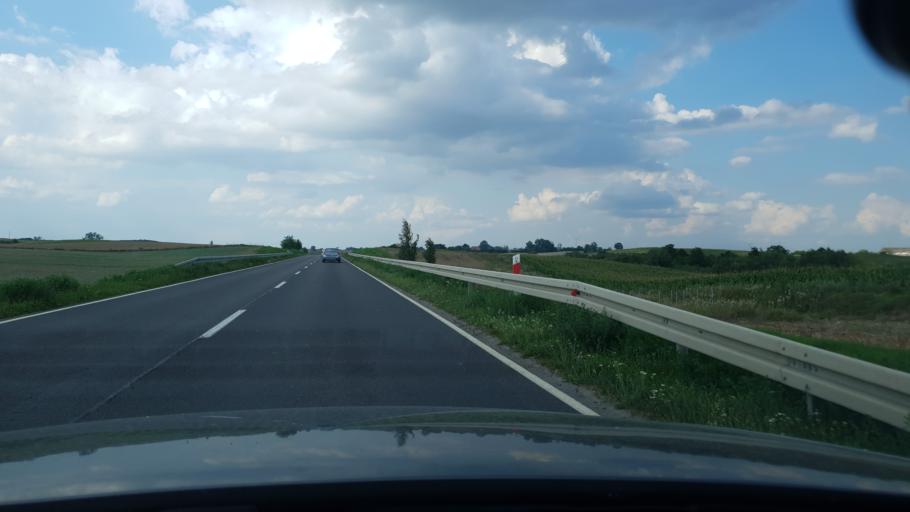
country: PL
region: Kujawsko-Pomorskie
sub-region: Powiat wabrzeski
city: Wabrzezno
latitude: 53.2975
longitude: 18.9262
